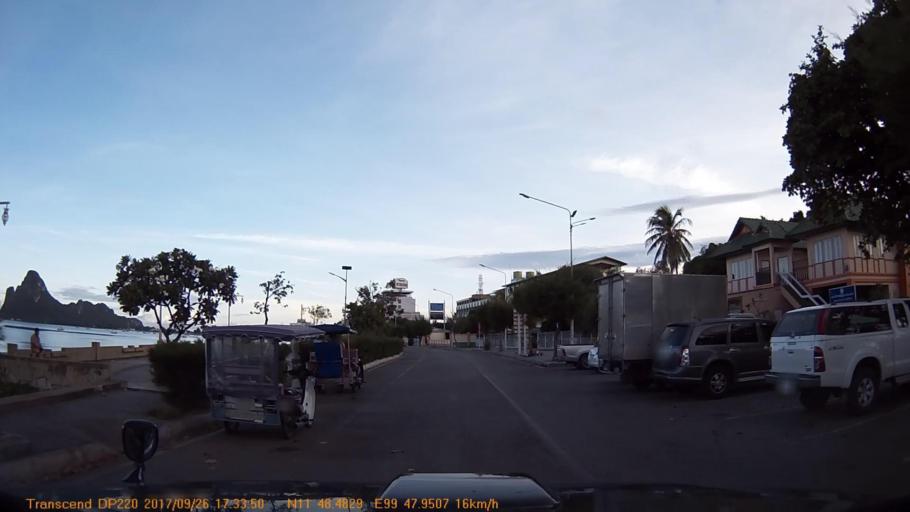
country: TH
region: Prachuap Khiri Khan
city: Prachuap Khiri Khan
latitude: 11.8080
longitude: 99.7992
